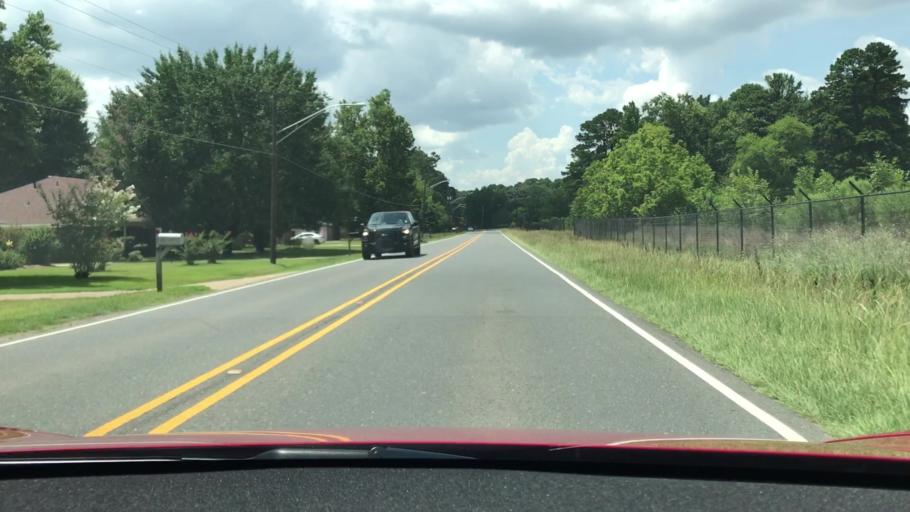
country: US
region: Louisiana
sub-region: Bossier Parish
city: Bossier City
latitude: 32.3882
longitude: -93.7196
